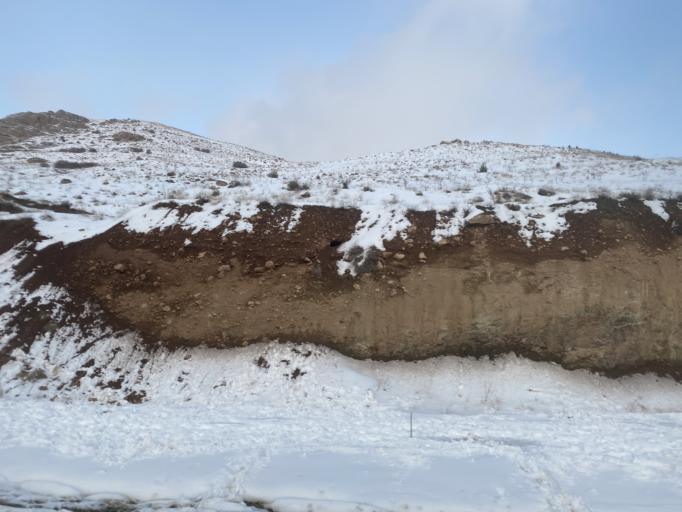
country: IR
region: Tehran
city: Damavand
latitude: 35.7831
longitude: 51.9554
